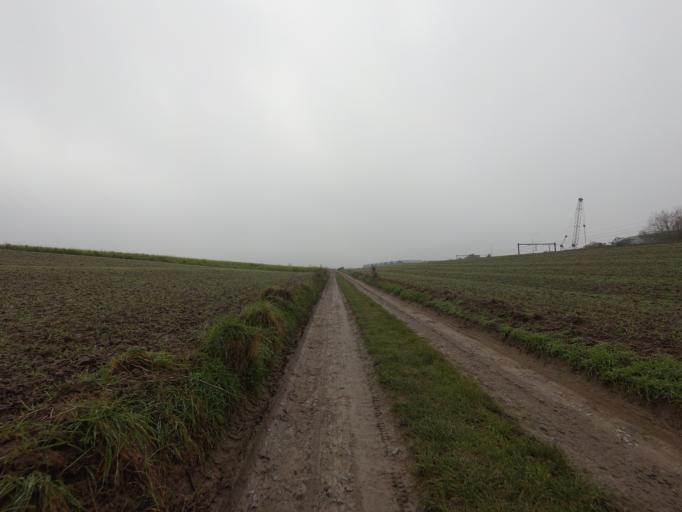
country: BE
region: Flanders
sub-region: Provincie Oost-Vlaanderen
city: Geraardsbergen
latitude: 50.7887
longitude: 3.8804
